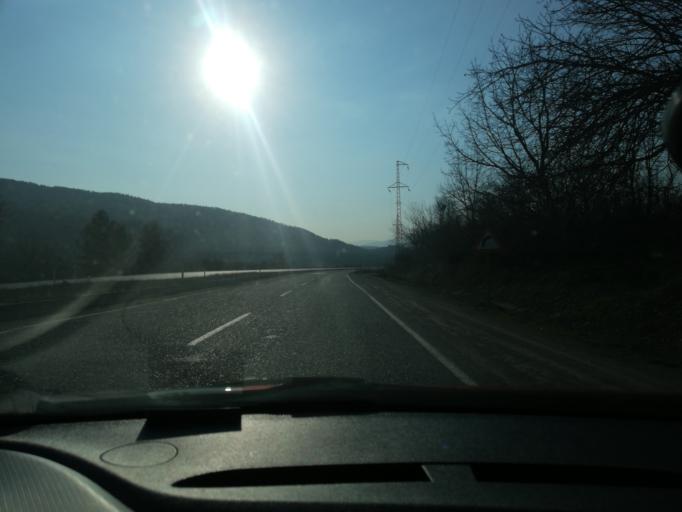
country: TR
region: Karabuk
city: Safranbolu
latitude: 41.2175
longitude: 32.7389
